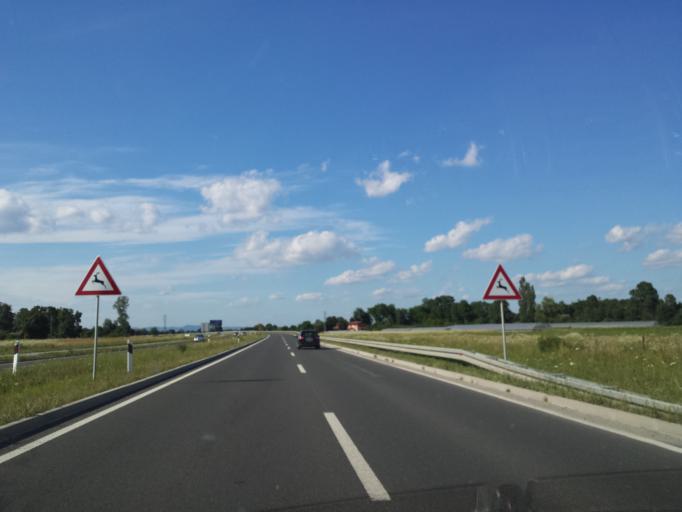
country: HR
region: Zagrebacka
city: Micevec
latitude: 45.7422
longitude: 16.1060
